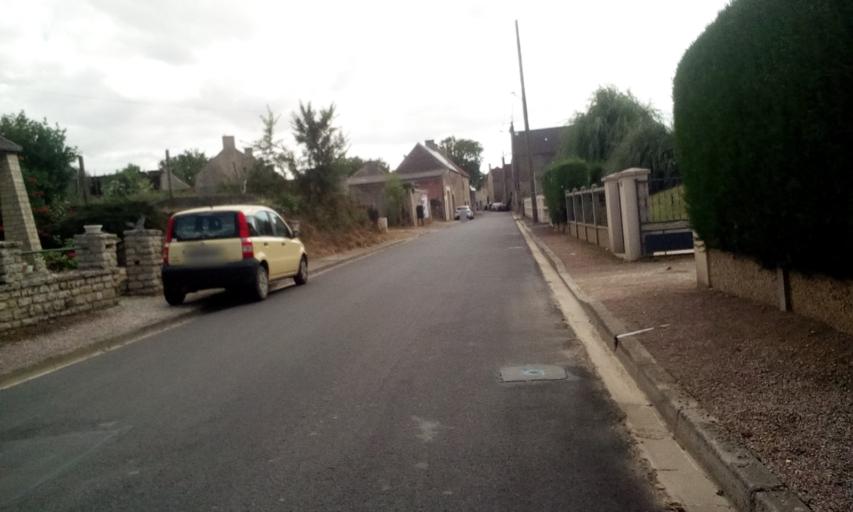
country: FR
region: Lower Normandy
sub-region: Departement du Calvados
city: Courseulles-sur-Mer
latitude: 49.3086
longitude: -0.4925
